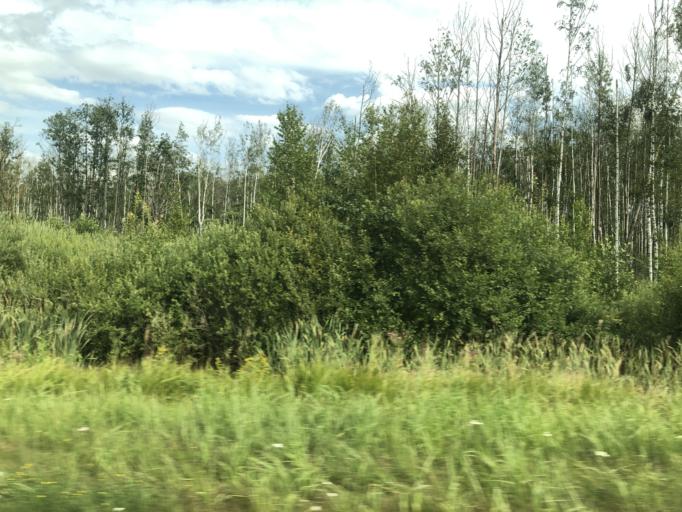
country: LV
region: Vecumnieki
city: Vecumnieki
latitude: 56.5083
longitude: 24.5650
